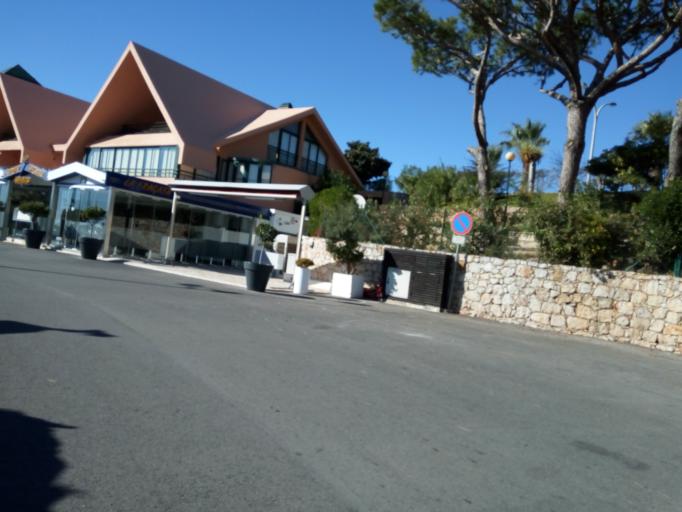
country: PT
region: Faro
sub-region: Loule
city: Vilamoura
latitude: 37.0793
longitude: -8.1199
